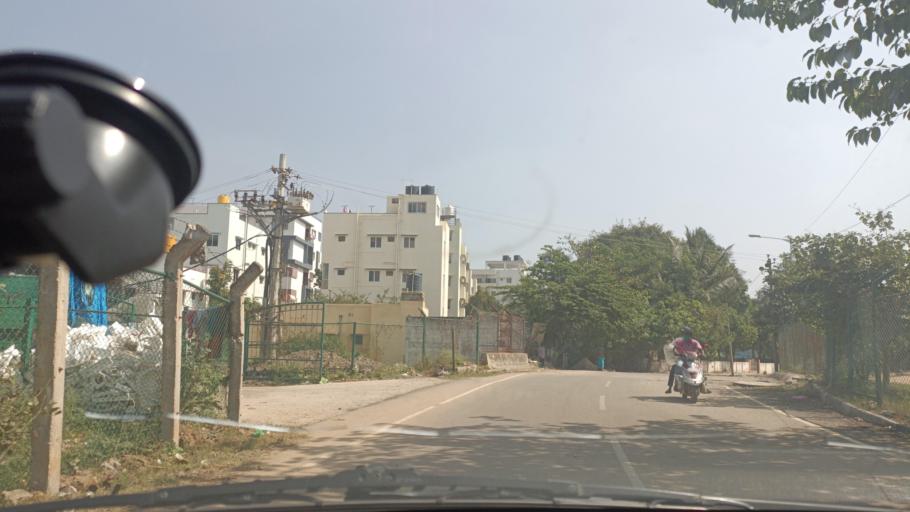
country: IN
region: Karnataka
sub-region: Bangalore Urban
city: Yelahanka
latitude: 13.1178
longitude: 77.6161
